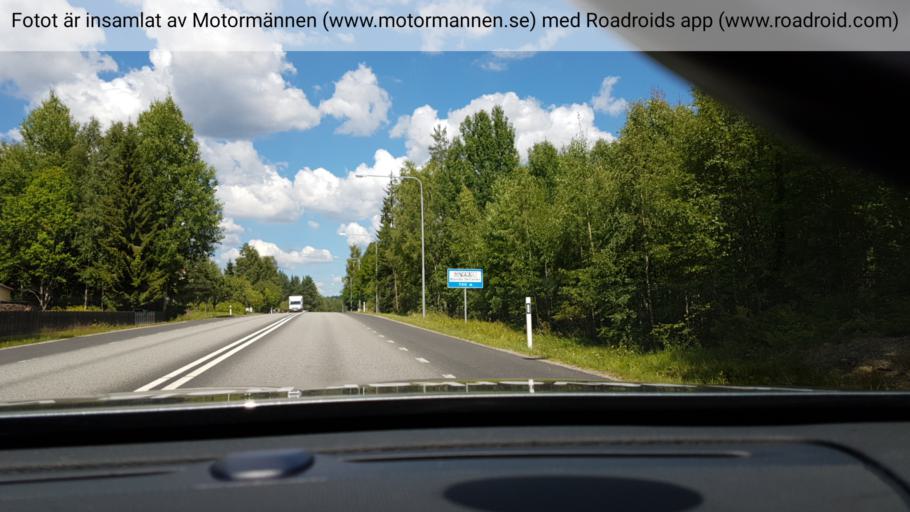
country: SE
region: Dalarna
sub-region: Faluns Kommun
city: Bjursas
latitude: 60.7280
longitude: 15.4452
